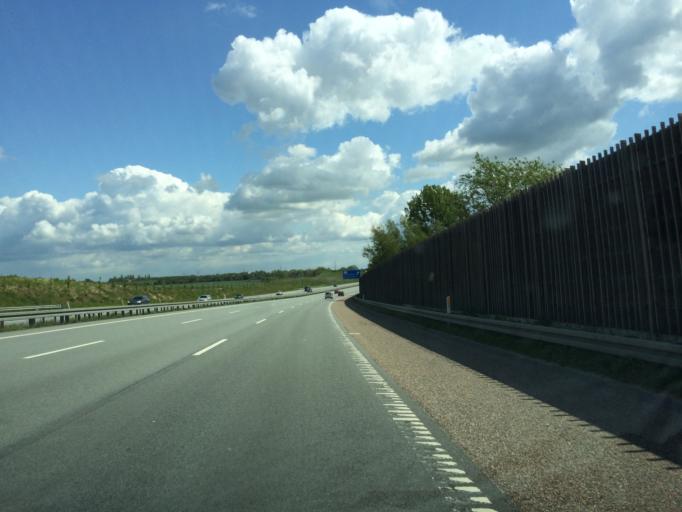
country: DK
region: Zealand
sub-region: Roskilde Kommune
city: Vindinge
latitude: 55.6504
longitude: 12.1479
